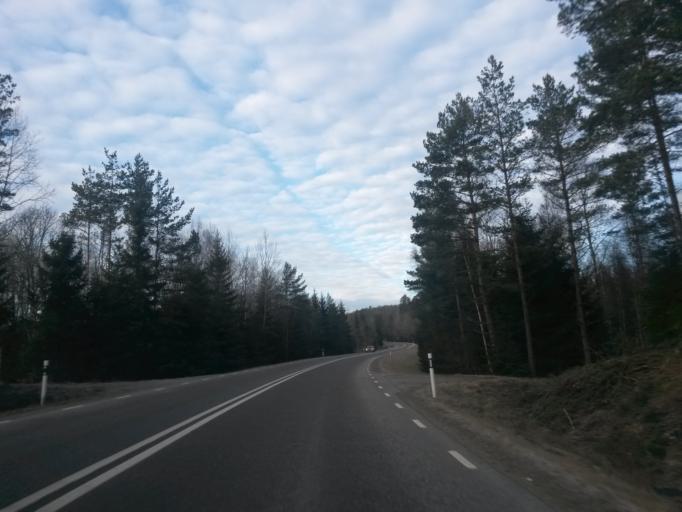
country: SE
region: Vaestra Goetaland
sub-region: Vargarda Kommun
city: Vargarda
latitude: 57.9438
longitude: 12.8381
